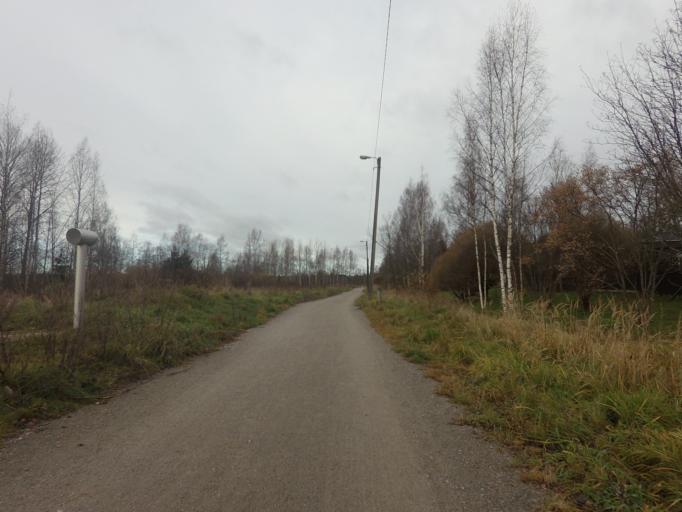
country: FI
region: Uusimaa
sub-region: Helsinki
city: Kauniainen
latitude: 60.1722
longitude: 24.7029
